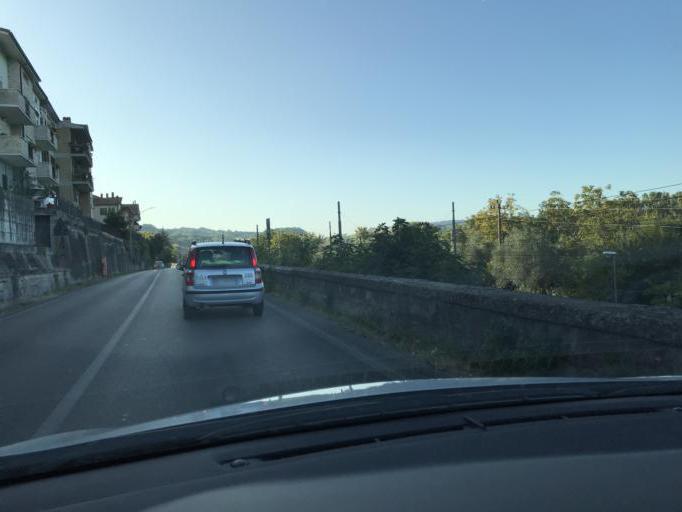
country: IT
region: Latium
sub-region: Provincia di Viterbo
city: Orte Scalo
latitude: 42.4428
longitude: 12.4055
